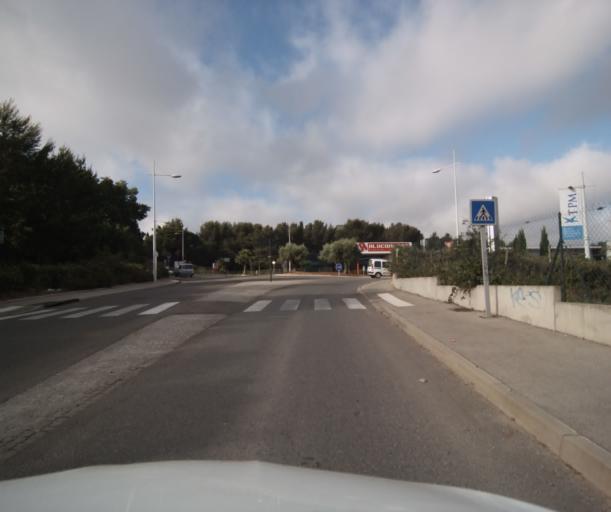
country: FR
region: Provence-Alpes-Cote d'Azur
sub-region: Departement du Var
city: Six-Fours-les-Plages
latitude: 43.1113
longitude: 5.8466
